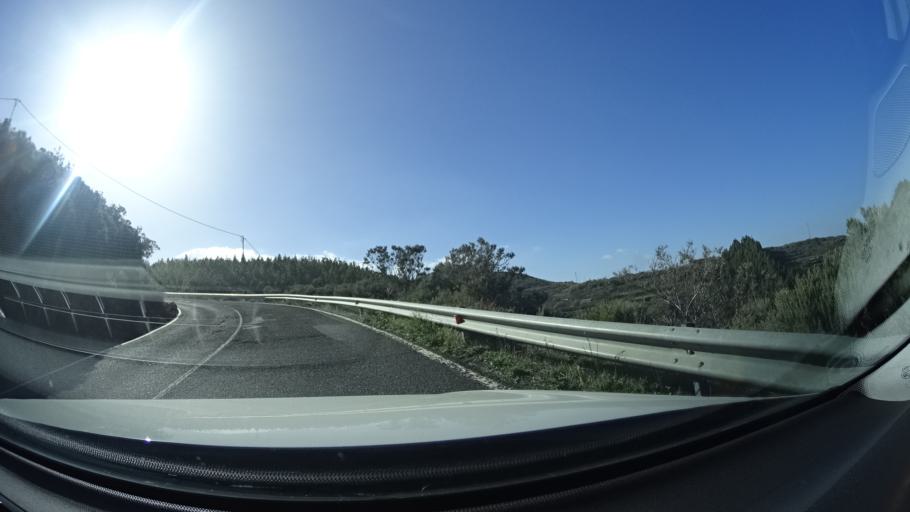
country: ES
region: Canary Islands
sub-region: Provincia de Las Palmas
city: San Bartolome
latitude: 27.9648
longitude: -15.5498
